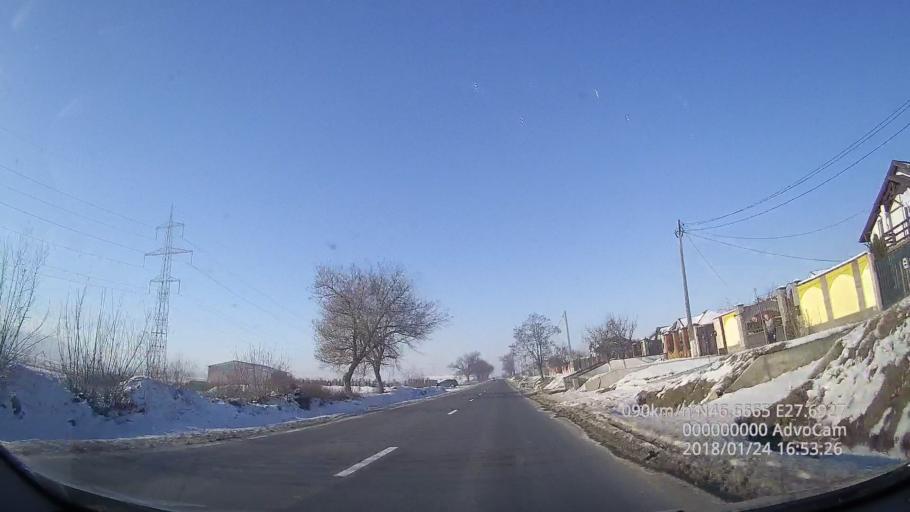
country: RO
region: Vaslui
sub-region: Municipiul Vaslui
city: Brodoc
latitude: 46.6669
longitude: 27.6921
